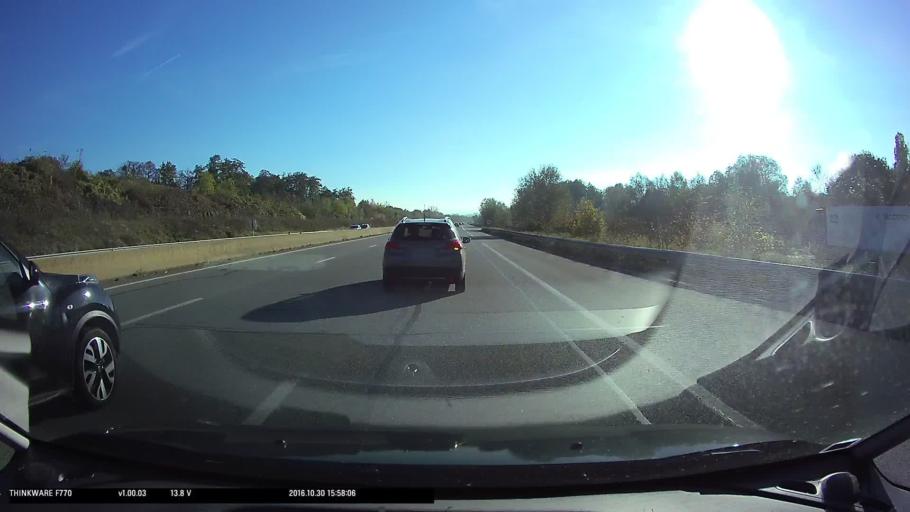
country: FR
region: Franche-Comte
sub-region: Departement du Doubs
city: Nommay
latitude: 47.5424
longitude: 6.8629
